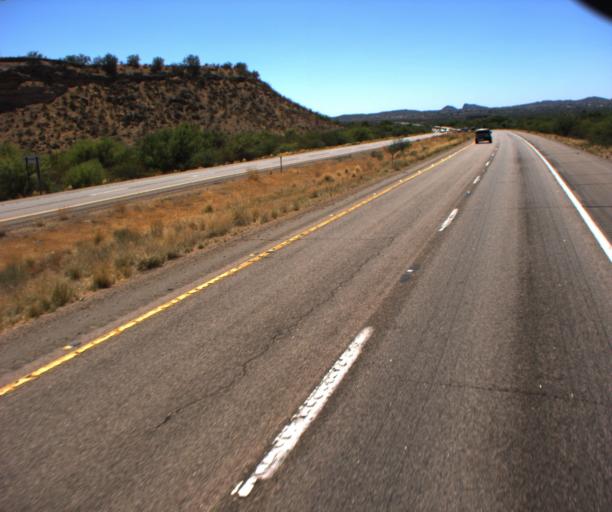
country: US
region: Arizona
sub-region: Maricopa County
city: Fountain Hills
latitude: 33.5826
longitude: -111.6580
